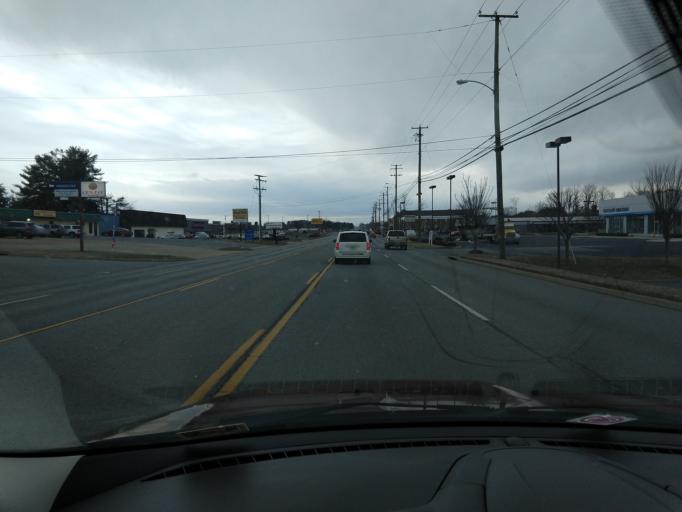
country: US
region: Virginia
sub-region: City of Waynesboro
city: Waynesboro
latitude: 38.0790
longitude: -78.9211
